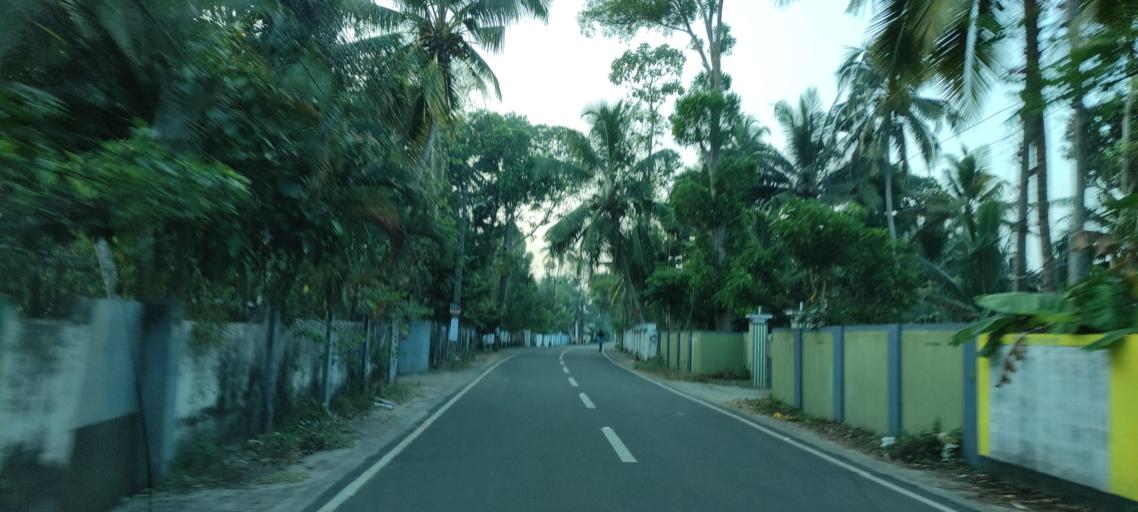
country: IN
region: Kerala
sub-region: Alappuzha
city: Alleppey
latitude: 9.4489
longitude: 76.3457
